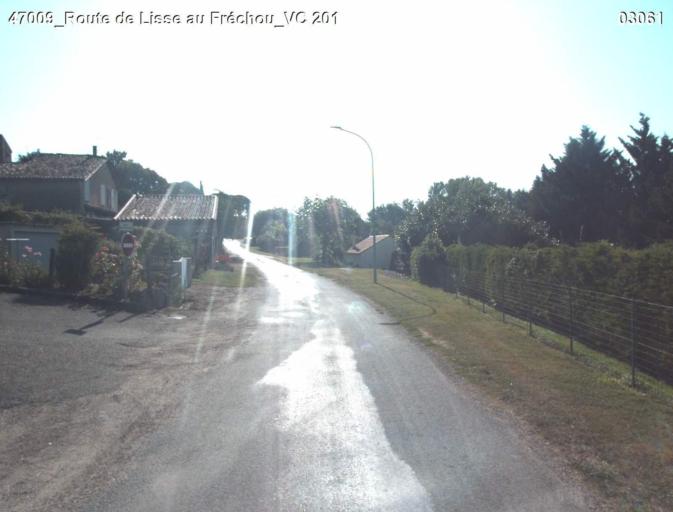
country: FR
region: Aquitaine
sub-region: Departement du Lot-et-Garonne
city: Mezin
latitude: 44.0973
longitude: 0.2757
